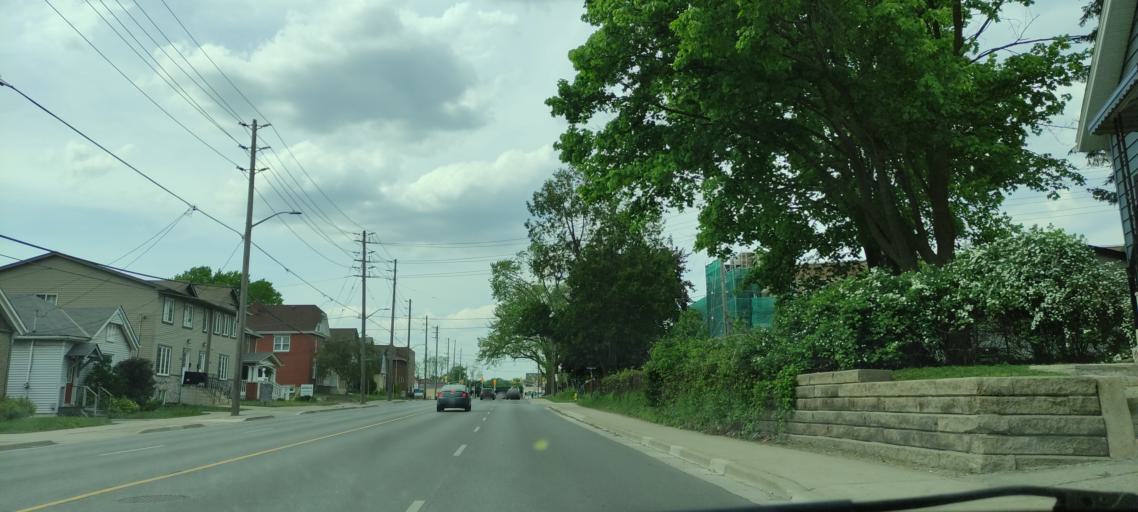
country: CA
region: Ontario
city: London
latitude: 42.9898
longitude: -81.2637
